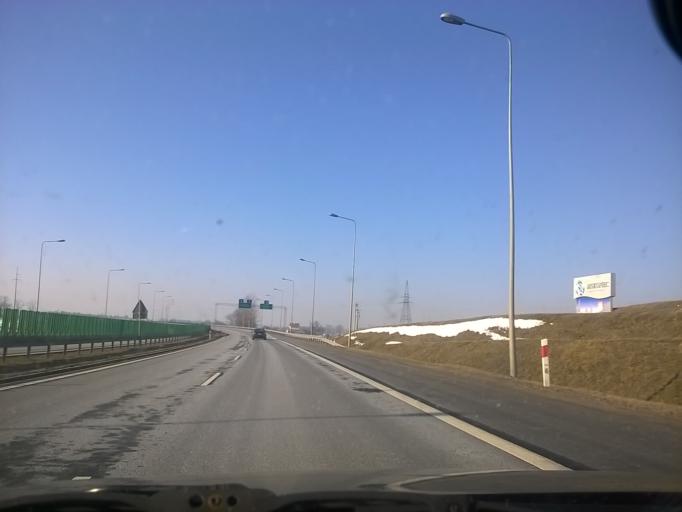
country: PL
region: Warmian-Masurian Voivodeship
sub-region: Powiat olsztynski
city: Biskupiec
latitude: 53.8486
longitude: 20.9750
